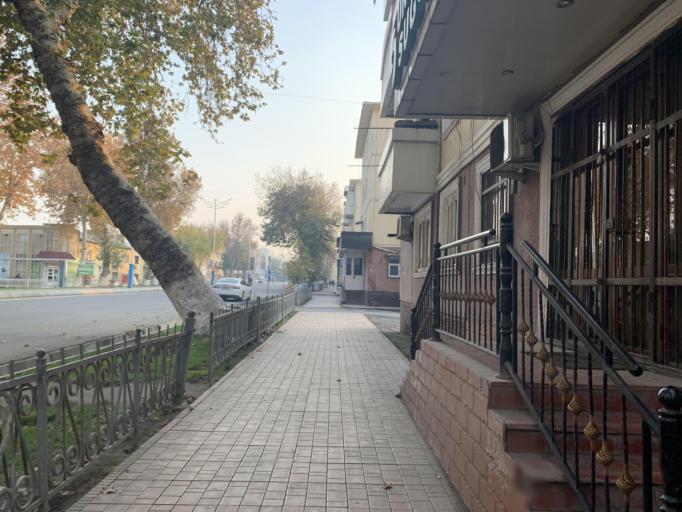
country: UZ
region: Fergana
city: Qo`qon
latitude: 40.5289
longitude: 70.9389
